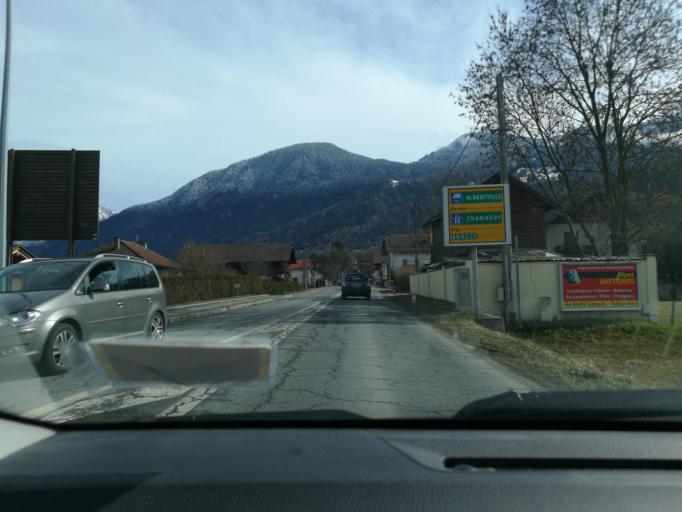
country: FR
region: Rhone-Alpes
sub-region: Departement de la Haute-Savoie
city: Passy
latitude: 45.9038
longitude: 6.6867
